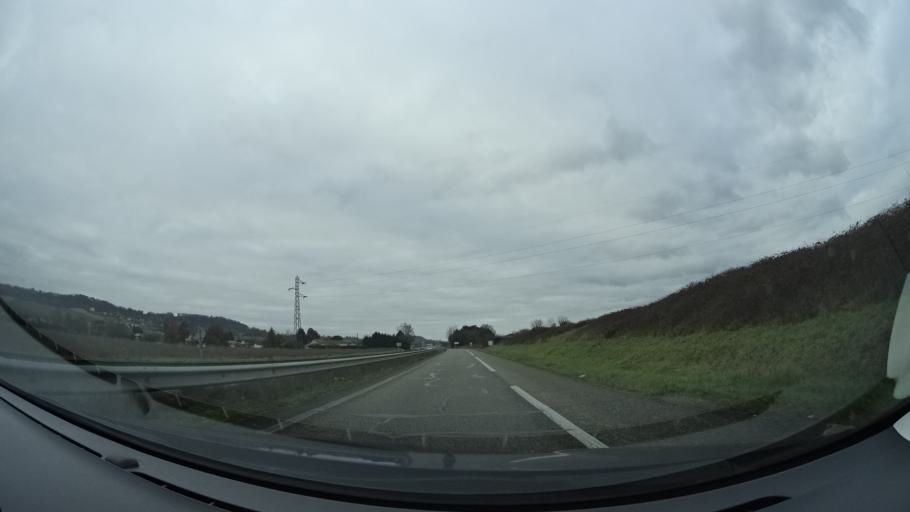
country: FR
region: Aquitaine
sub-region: Departement du Lot-et-Garonne
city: Sainte-Livrade-sur-Lot
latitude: 44.3982
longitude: 0.6102
